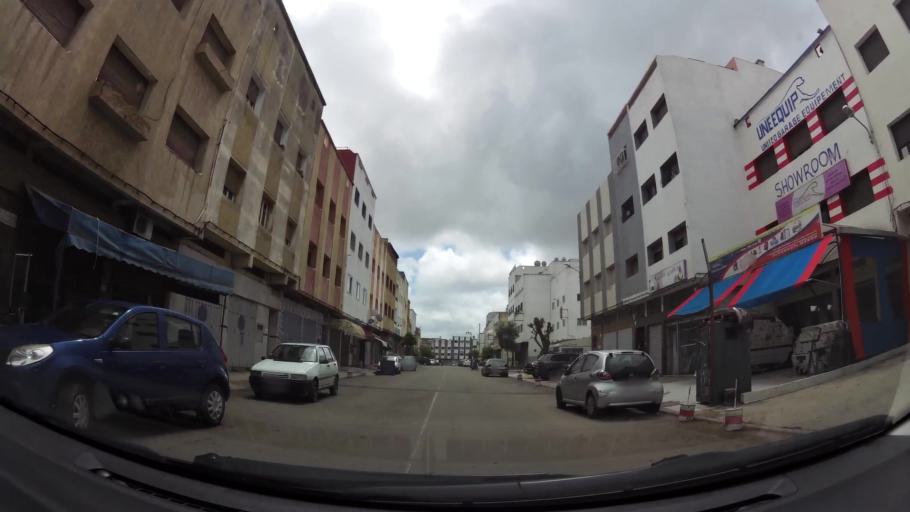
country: MA
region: Grand Casablanca
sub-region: Casablanca
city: Casablanca
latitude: 33.5549
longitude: -7.6841
